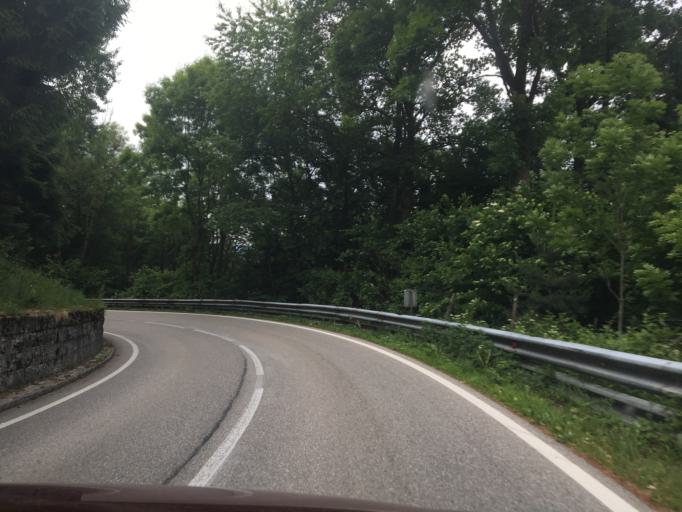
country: AT
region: Upper Austria
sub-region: Politischer Bezirk Grieskirchen
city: Grieskirchen
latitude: 48.3684
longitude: 13.8701
